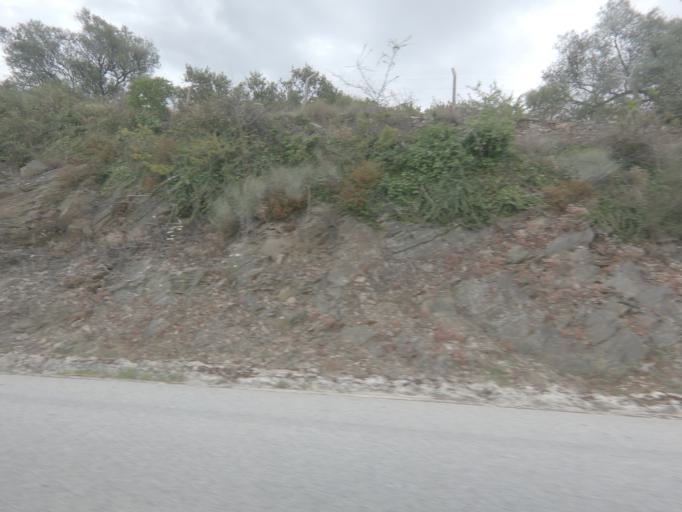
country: PT
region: Viseu
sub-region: Armamar
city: Armamar
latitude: 41.1111
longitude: -7.6859
